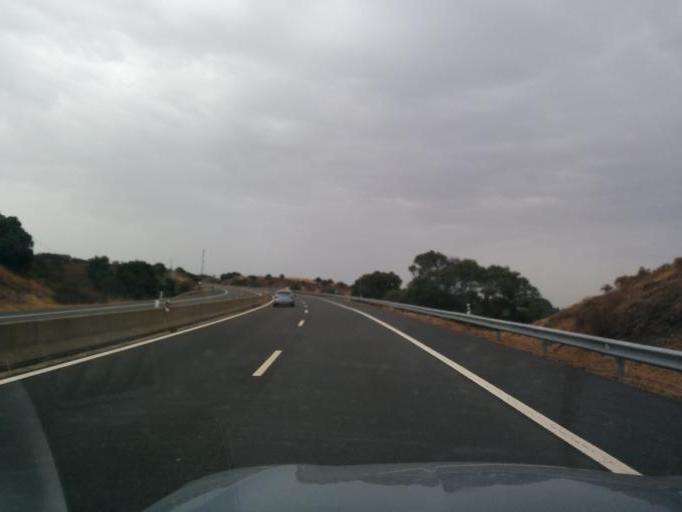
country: PT
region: Faro
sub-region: Tavira
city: Tavira
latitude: 37.1798
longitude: -7.5802
